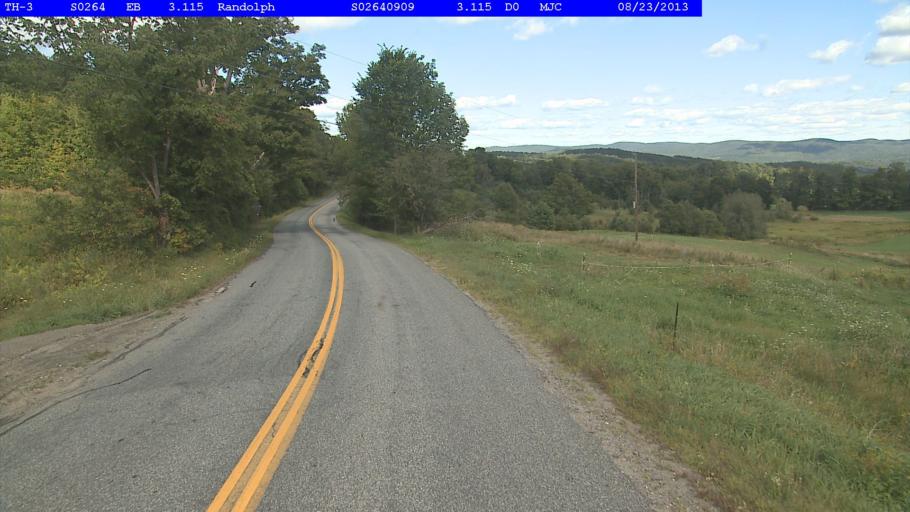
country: US
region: Vermont
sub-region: Orange County
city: Chelsea
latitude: 43.9623
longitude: -72.5185
